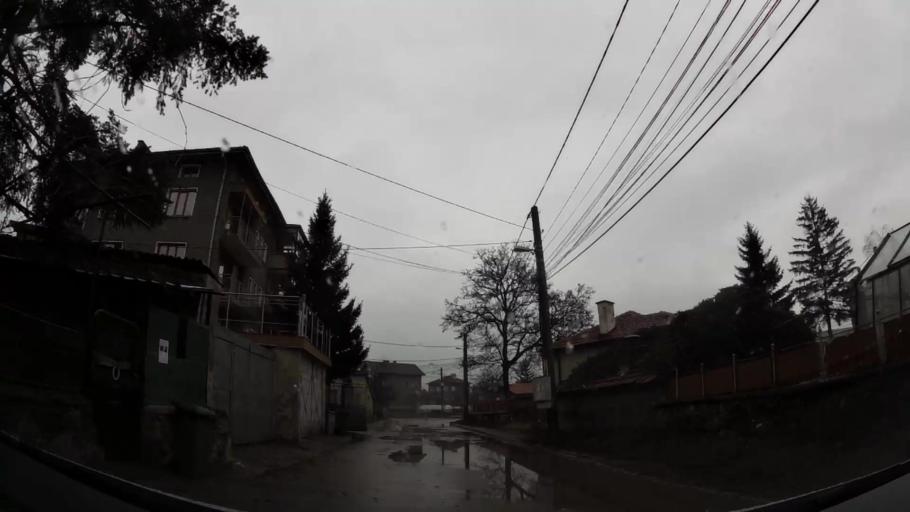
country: BG
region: Sofia-Capital
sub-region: Stolichna Obshtina
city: Sofia
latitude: 42.6303
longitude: 23.4050
